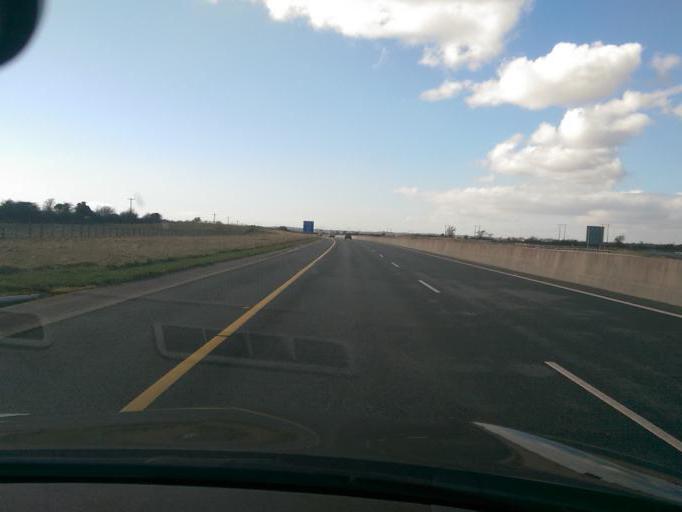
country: IE
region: Connaught
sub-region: County Galway
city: Oranmore
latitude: 53.2995
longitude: -8.8819
